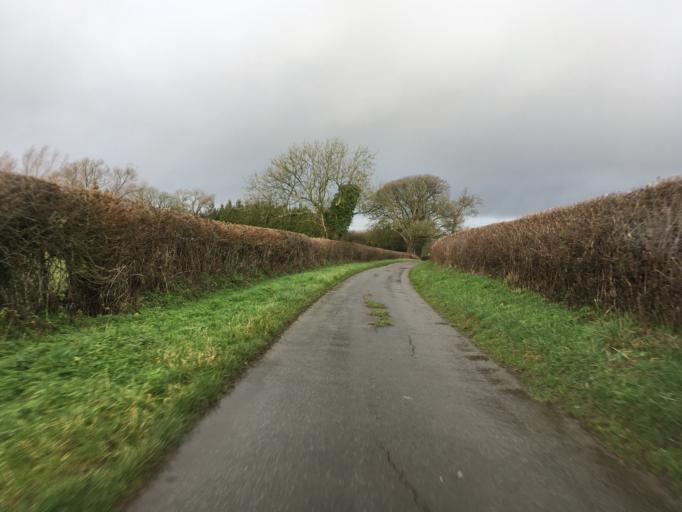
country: GB
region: England
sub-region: Wiltshire
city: Hankerton
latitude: 51.6388
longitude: -2.0763
